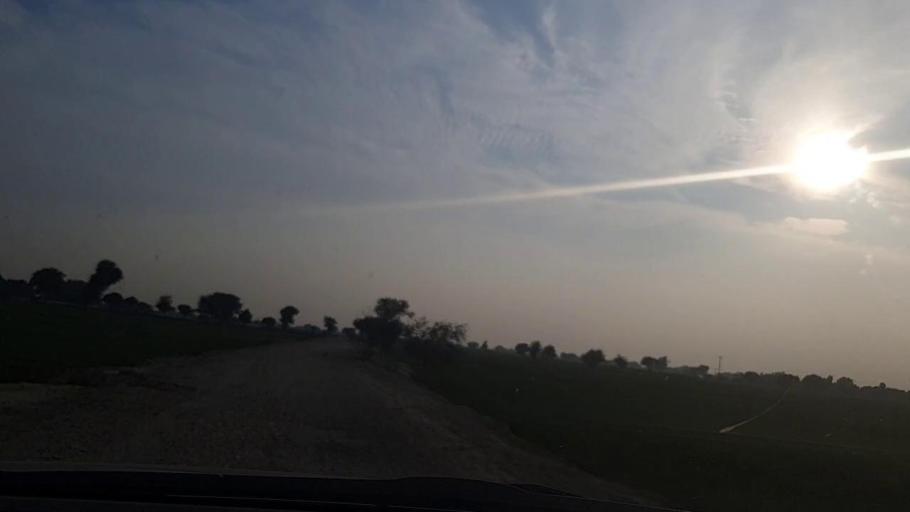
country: PK
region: Sindh
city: Daulatpur
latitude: 26.3344
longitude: 68.0234
